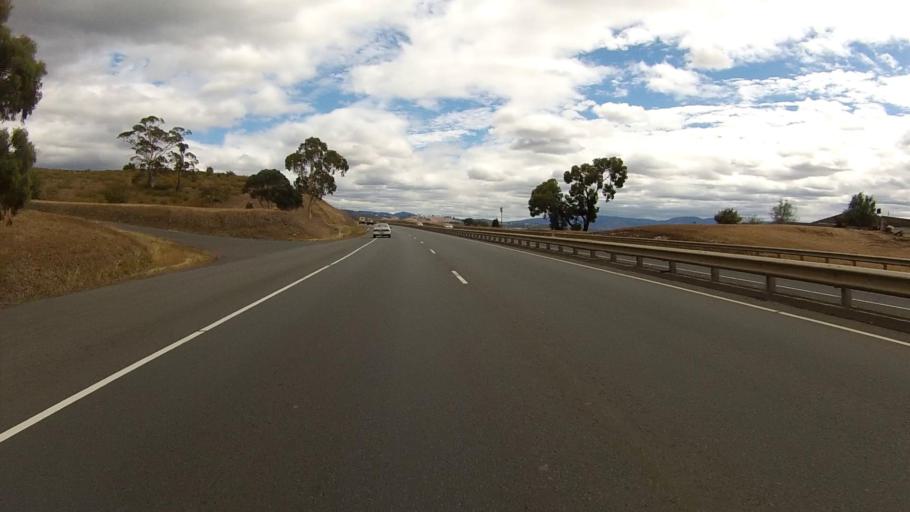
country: AU
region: Tasmania
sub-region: Glenorchy
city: Austins Ferry
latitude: -42.7647
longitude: 147.2351
